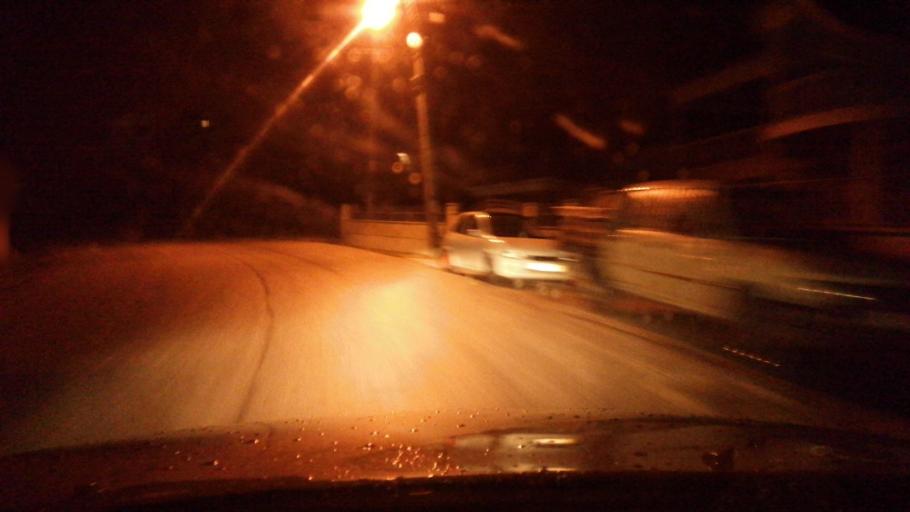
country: PT
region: Viseu
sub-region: Armamar
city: Armamar
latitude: 41.0676
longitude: -7.6458
